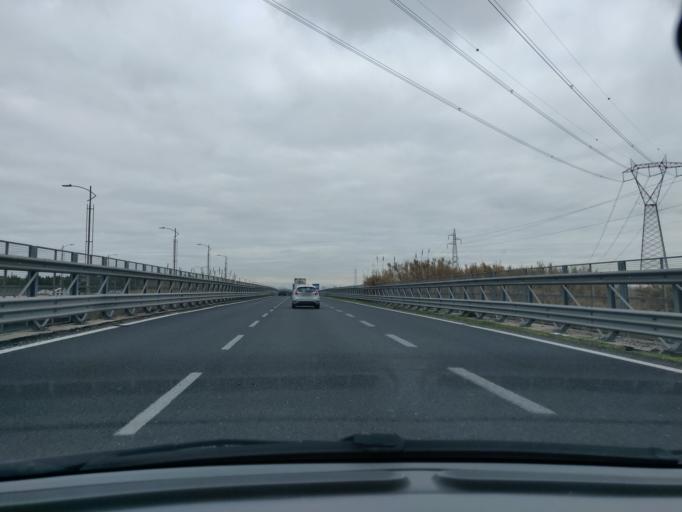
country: IT
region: Latium
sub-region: Citta metropolitana di Roma Capitale
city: Ponte Galeria-La Pisana
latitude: 41.8141
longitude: 12.3350
